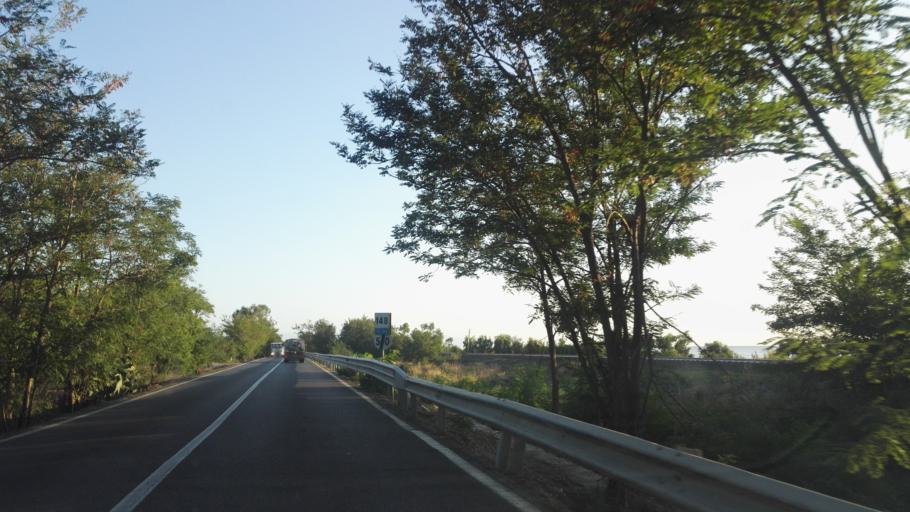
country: IT
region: Calabria
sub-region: Provincia di Catanzaro
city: Santa Caterina dello Ionio Marina
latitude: 38.5479
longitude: 16.5701
